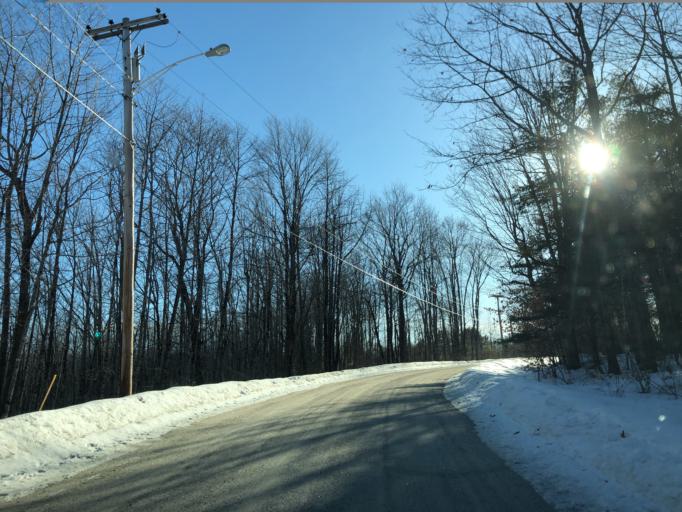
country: US
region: Maine
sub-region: Androscoggin County
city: Poland
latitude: 44.0283
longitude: -70.3589
